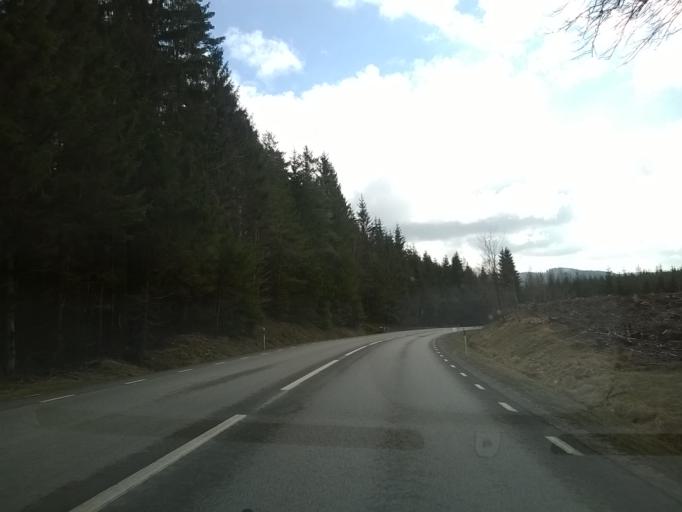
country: SE
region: Vaestra Goetaland
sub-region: Marks Kommun
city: Horred
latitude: 57.1568
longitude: 12.6690
